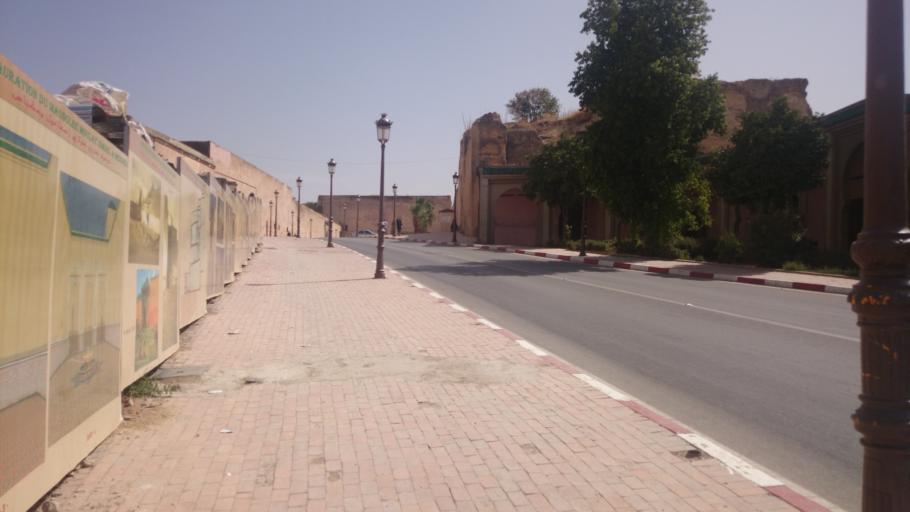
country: MA
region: Meknes-Tafilalet
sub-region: Meknes
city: Meknes
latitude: 33.8906
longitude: -5.5634
